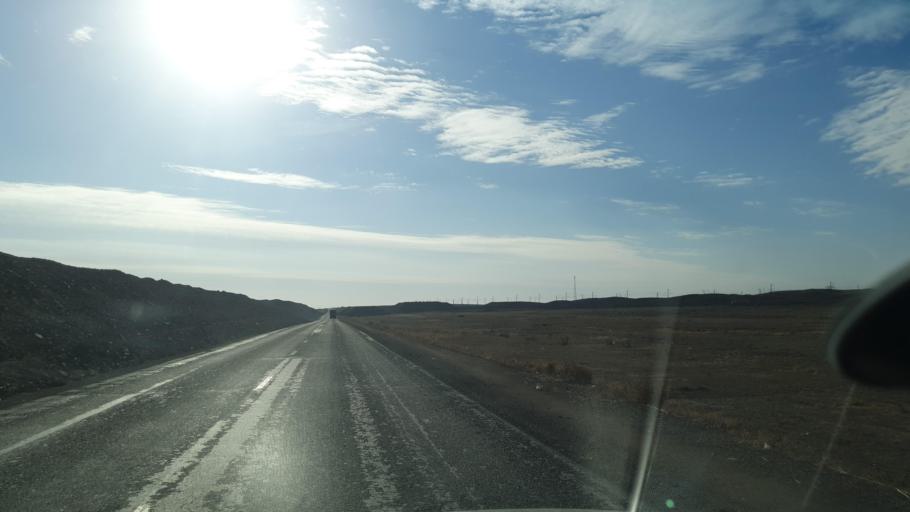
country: KZ
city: Priozersk
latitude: 45.8289
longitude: 73.4504
